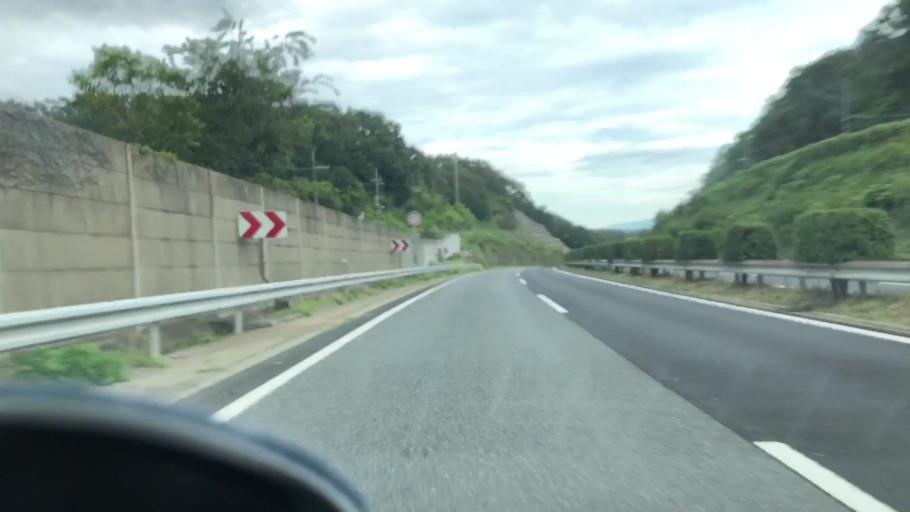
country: JP
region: Hyogo
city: Yashiro
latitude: 34.8921
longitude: 135.0900
